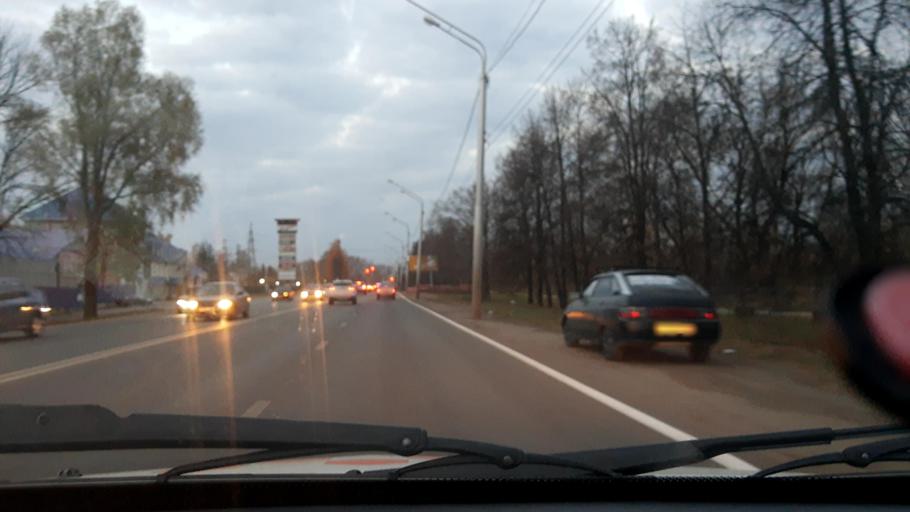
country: RU
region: Bashkortostan
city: Avdon
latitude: 54.6948
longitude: 55.8259
